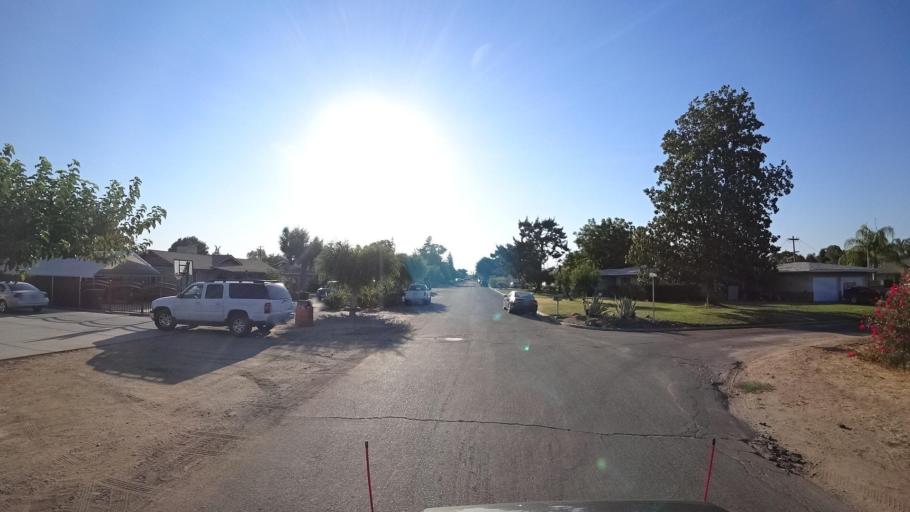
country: US
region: California
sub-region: Fresno County
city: Sunnyside
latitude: 36.7371
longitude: -119.7077
